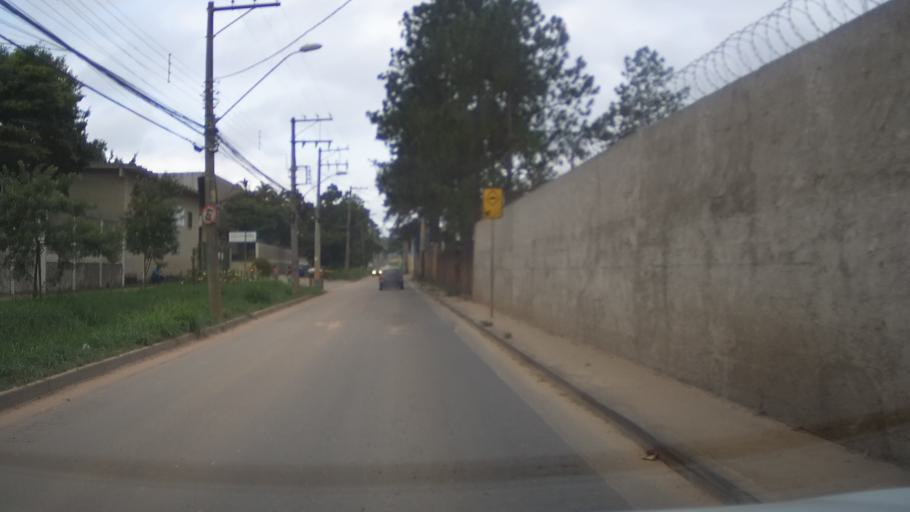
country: BR
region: Sao Paulo
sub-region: Aruja
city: Aruja
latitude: -23.4111
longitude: -46.3848
